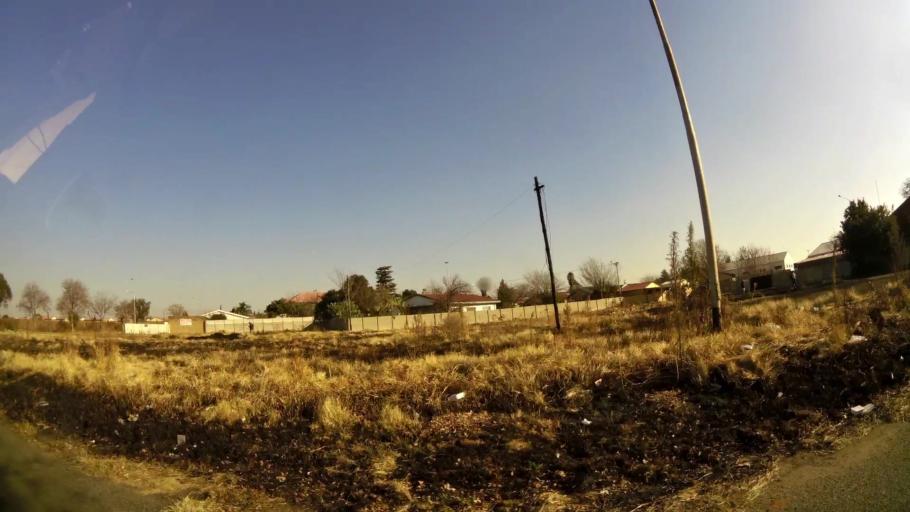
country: ZA
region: Gauteng
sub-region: West Rand District Municipality
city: Randfontein
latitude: -26.1951
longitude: 27.7011
